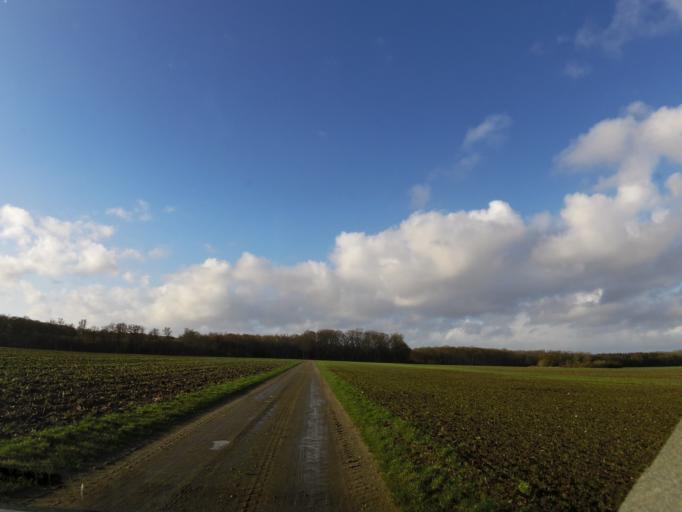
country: DK
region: Central Jutland
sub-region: Odder Kommune
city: Odder
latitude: 55.8518
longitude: 10.1741
